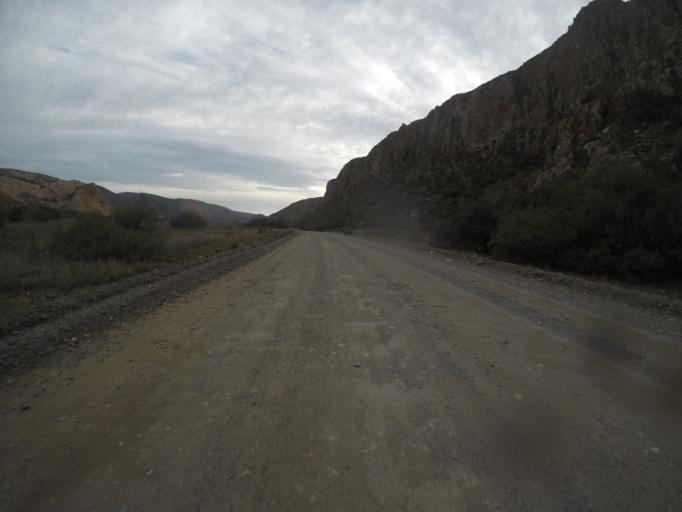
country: ZA
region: Eastern Cape
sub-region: Cacadu District Municipality
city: Willowmore
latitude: -33.5194
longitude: 23.6721
